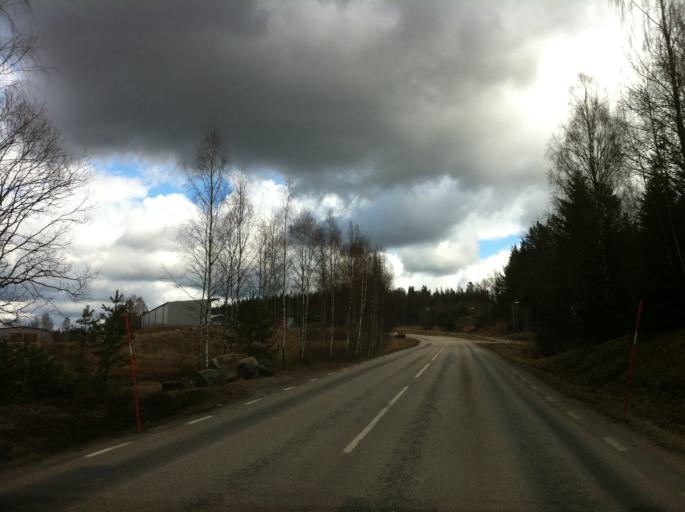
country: SE
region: Joenkoeping
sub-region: Gislaveds Kommun
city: Smalandsstenar
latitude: 57.2666
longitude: 13.2341
